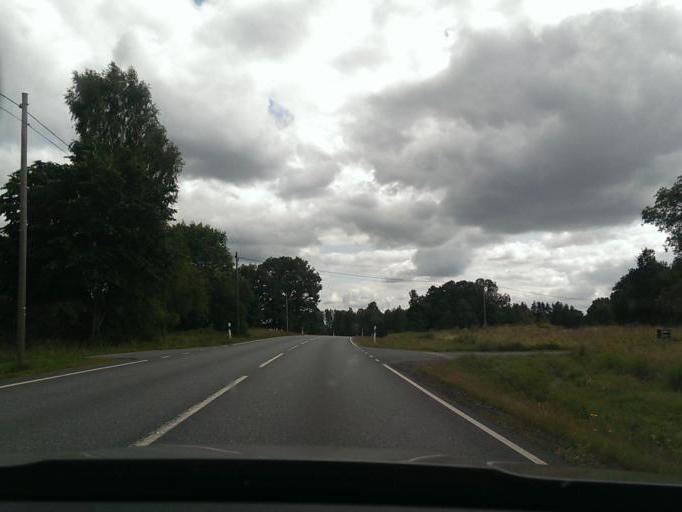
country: SE
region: Joenkoeping
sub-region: Varnamo Kommun
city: Varnamo
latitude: 57.2388
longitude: 14.0040
